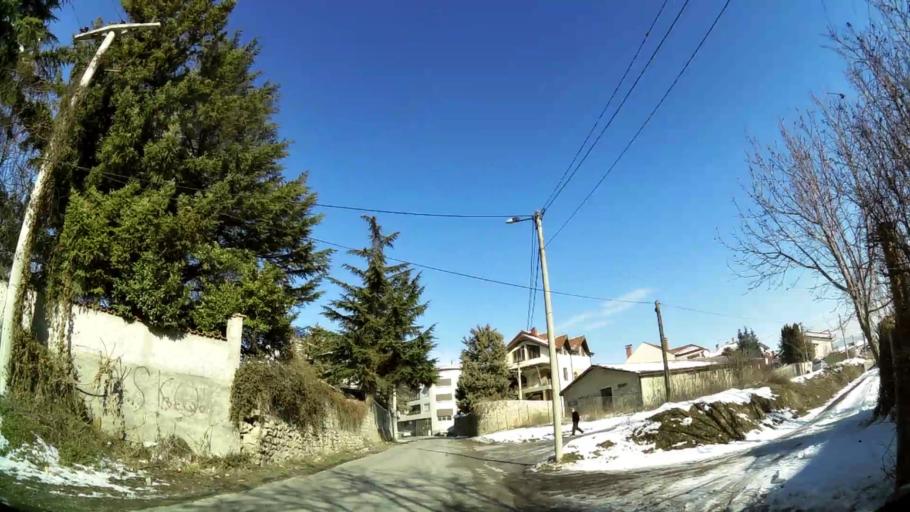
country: MK
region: Saraj
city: Saraj
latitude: 41.9968
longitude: 21.3262
